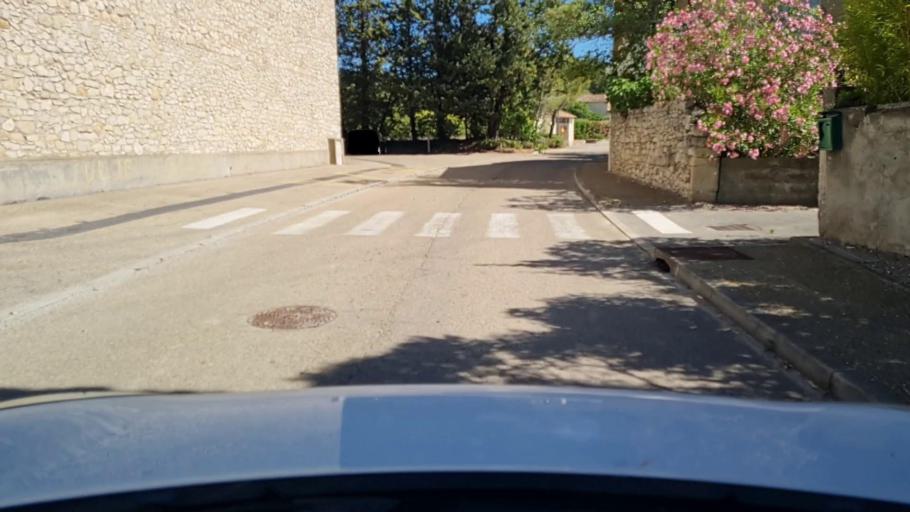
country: FR
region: Languedoc-Roussillon
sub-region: Departement du Gard
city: Villevieille
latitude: 43.8579
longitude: 4.1146
